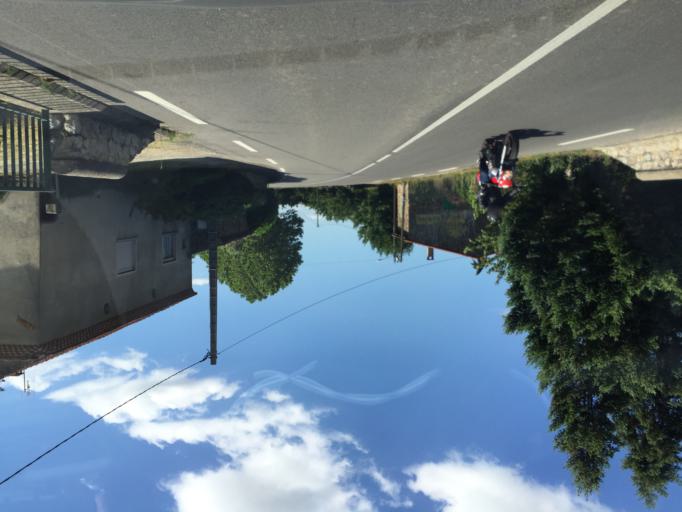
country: FR
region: Rhone-Alpes
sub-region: Departement de l'Ardeche
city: Saint-Jean-de-Muzols
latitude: 45.1017
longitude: 4.8175
